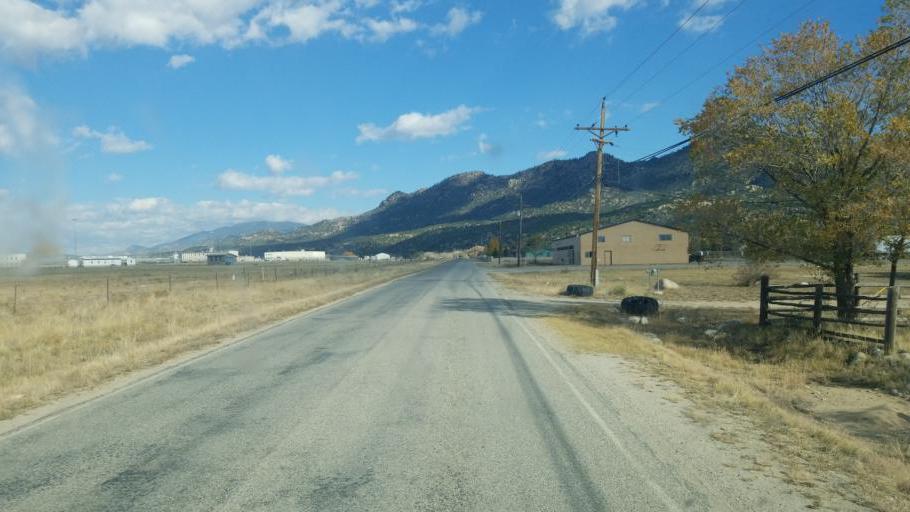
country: US
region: Colorado
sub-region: Chaffee County
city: Buena Vista
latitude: 38.8163
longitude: -106.1093
